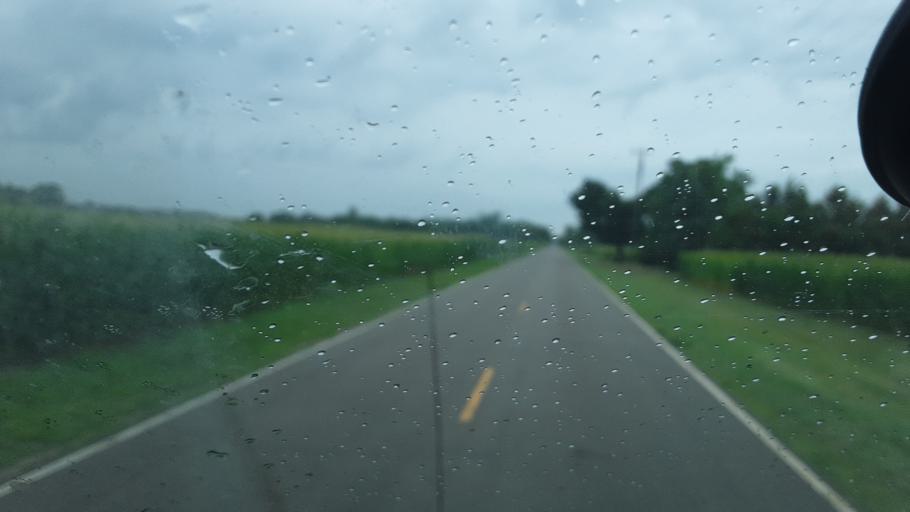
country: US
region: Ohio
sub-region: Williams County
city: Bryan
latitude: 41.3740
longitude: -84.6309
